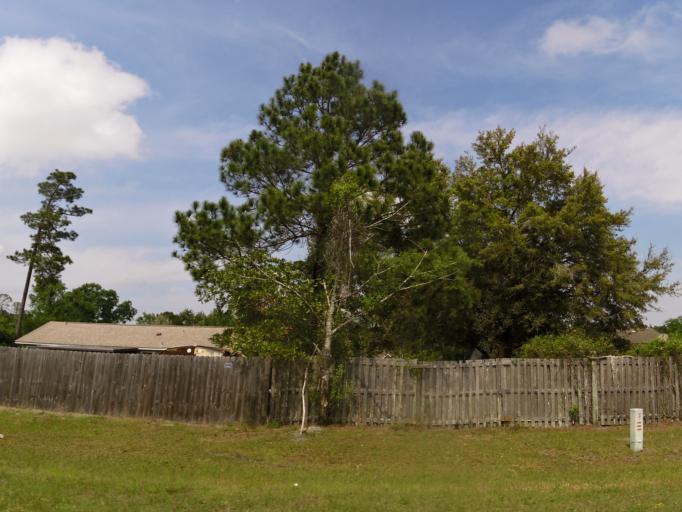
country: US
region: Georgia
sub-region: Camden County
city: Kingsland
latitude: 30.7739
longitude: -81.6738
